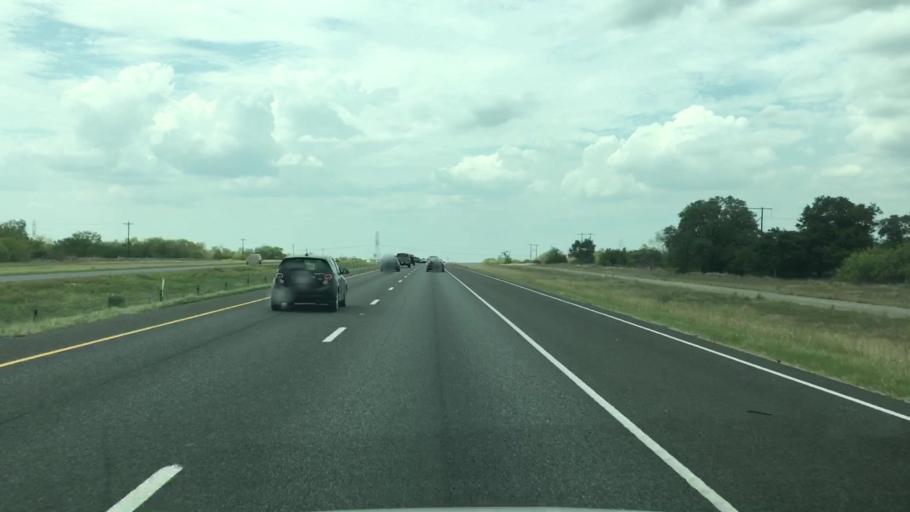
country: US
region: Texas
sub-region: Atascosa County
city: Pleasanton
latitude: 28.8143
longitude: -98.3552
